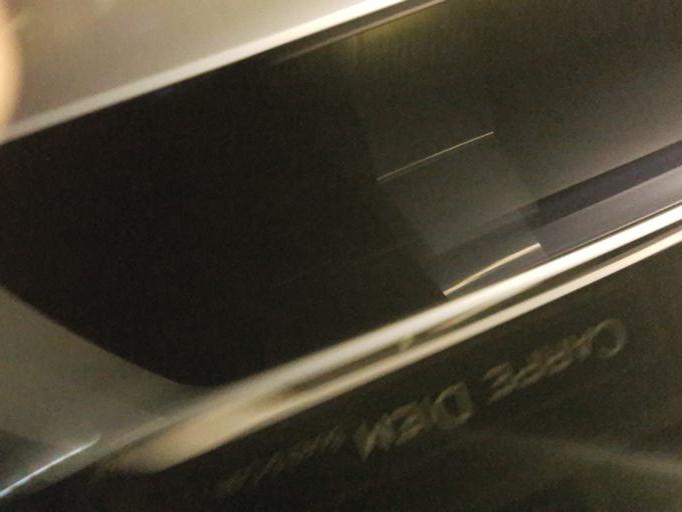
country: TW
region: Taiwan
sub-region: Hsinchu
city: Hsinchu
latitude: 24.8123
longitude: 120.9837
